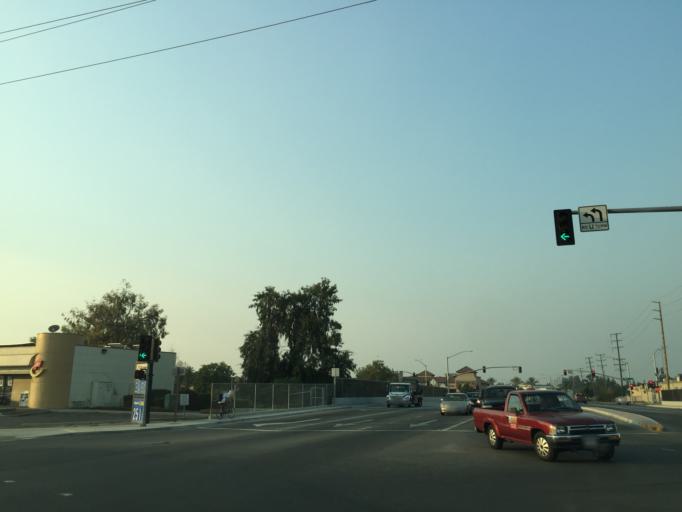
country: US
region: California
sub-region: Tulare County
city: Visalia
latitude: 36.3275
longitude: -119.2785
